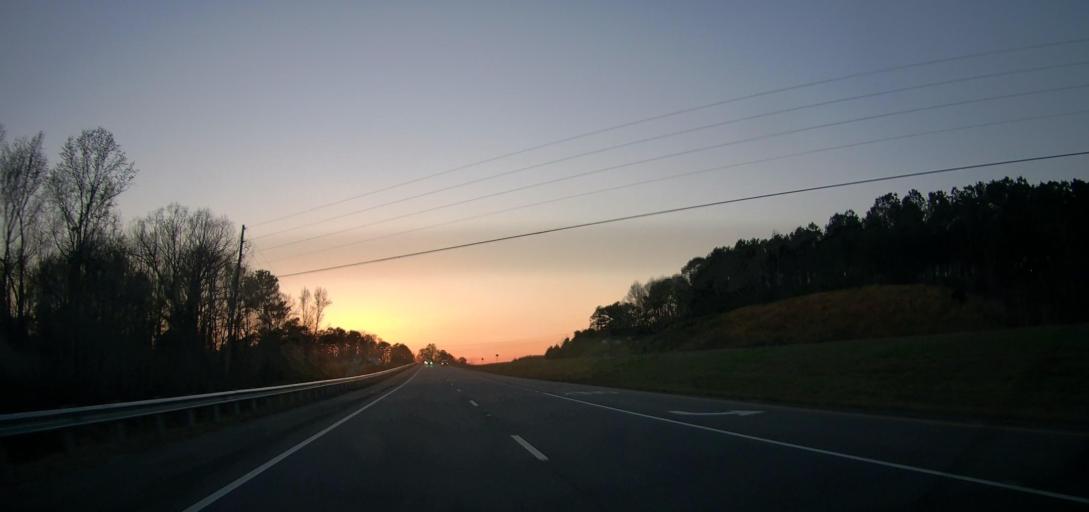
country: US
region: Alabama
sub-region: Tallapoosa County
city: Dadeville
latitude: 32.8805
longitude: -85.8470
